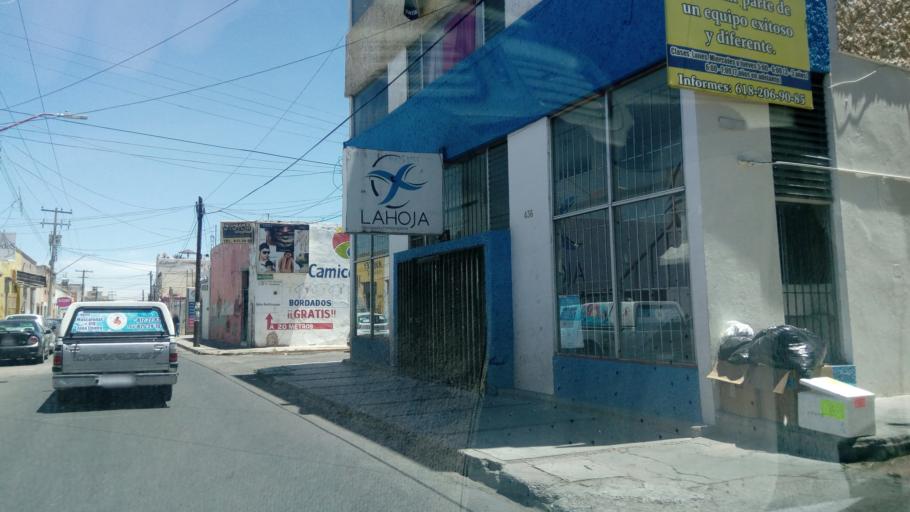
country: MX
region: Durango
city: Victoria de Durango
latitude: 24.0239
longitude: -104.6594
